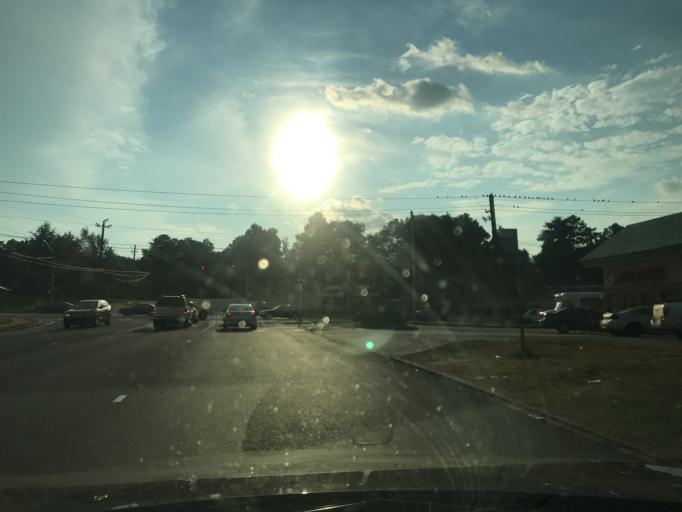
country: US
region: Georgia
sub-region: DeKalb County
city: Gresham Park
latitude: 33.7156
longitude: -84.3488
